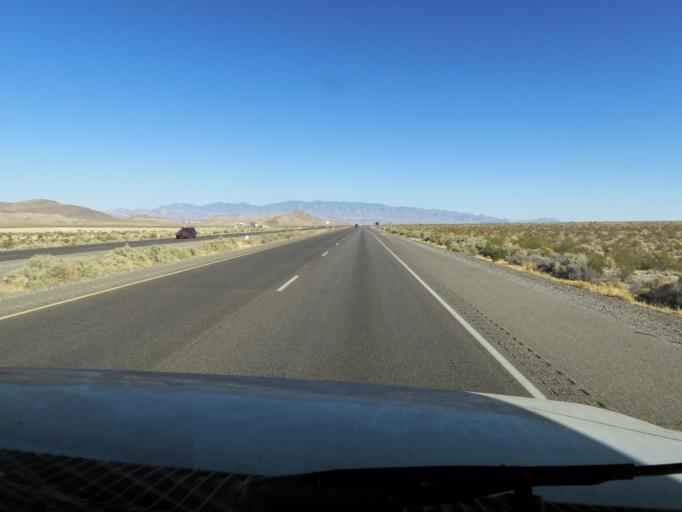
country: US
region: Nevada
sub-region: Nye County
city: Pahrump
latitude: 36.5767
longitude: -115.6523
